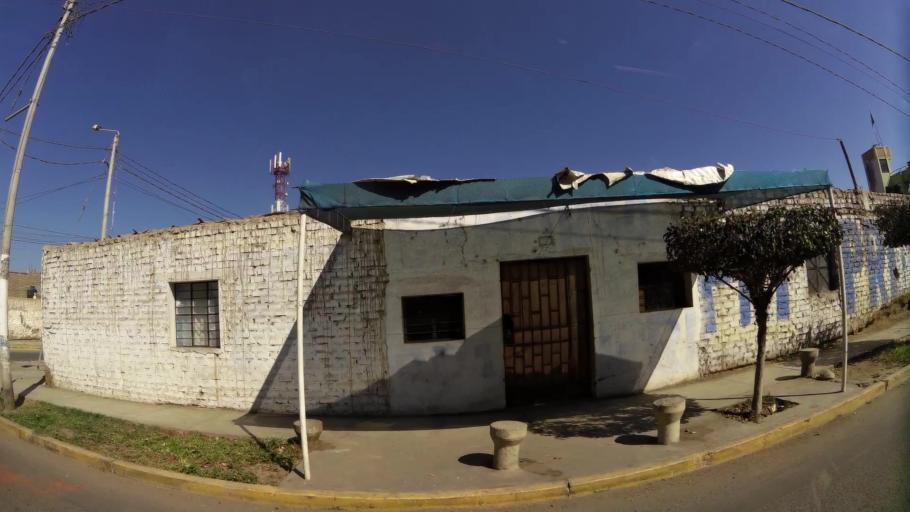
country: PE
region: Ica
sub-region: Provincia de Ica
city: La Tinguina
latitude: -14.0365
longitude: -75.7082
